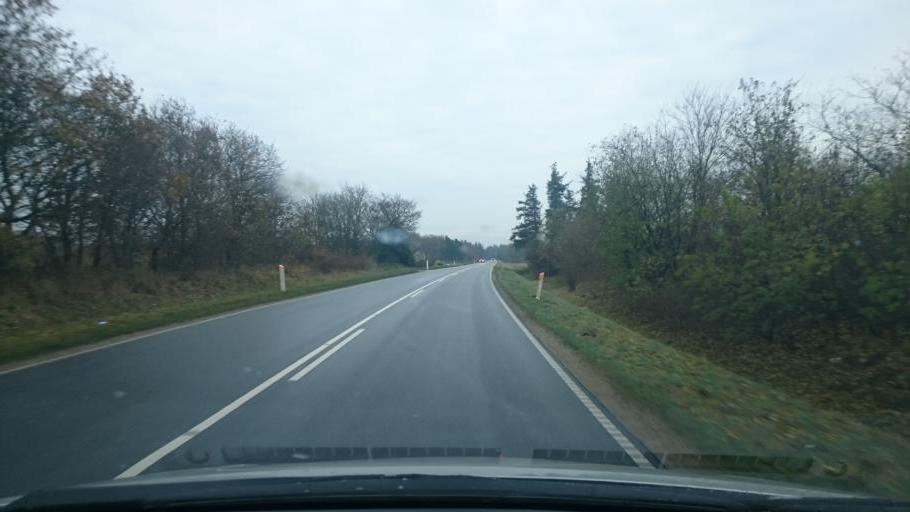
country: DK
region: South Denmark
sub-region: Esbjerg Kommune
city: Ribe
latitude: 55.3348
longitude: 8.8505
